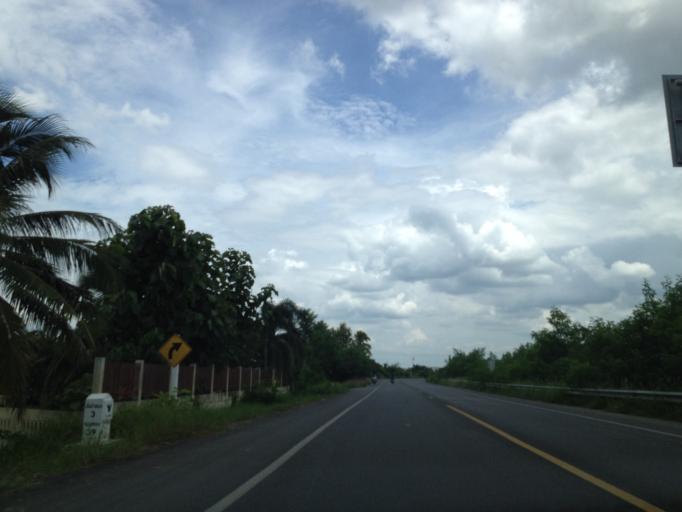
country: TH
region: Chiang Mai
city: San Pa Tong
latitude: 18.6308
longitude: 98.8802
